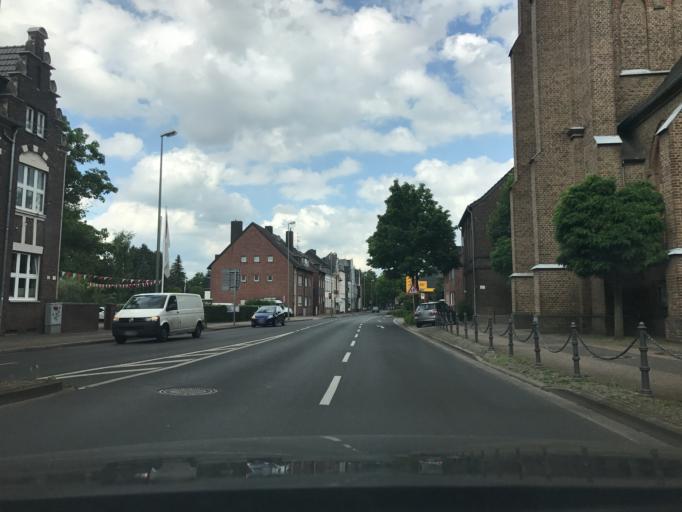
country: DE
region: North Rhine-Westphalia
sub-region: Regierungsbezirk Dusseldorf
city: Neuss
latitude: 51.2173
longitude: 6.6629
